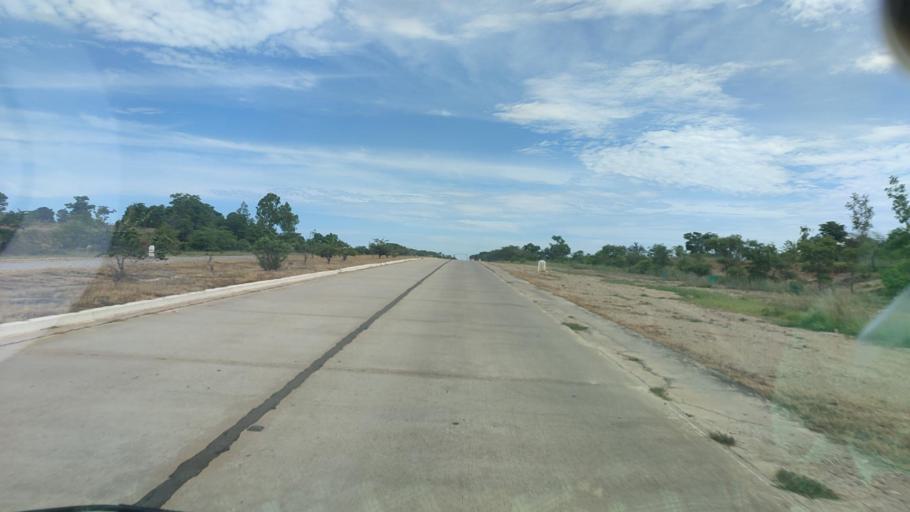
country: MM
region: Mandalay
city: Yamethin
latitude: 20.4735
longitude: 95.8287
